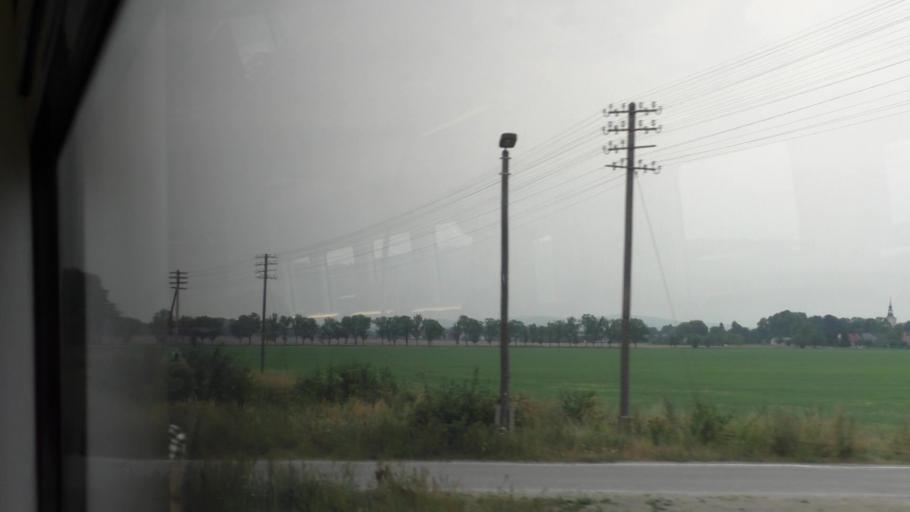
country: DE
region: Saxony
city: Horka
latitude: 51.2963
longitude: 14.9026
